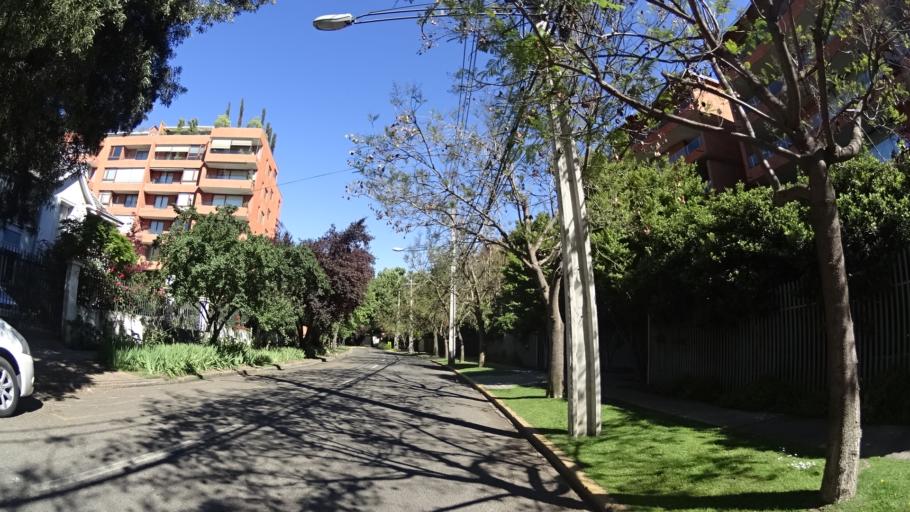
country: CL
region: Santiago Metropolitan
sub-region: Provincia de Santiago
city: Villa Presidente Frei, Nunoa, Santiago, Chile
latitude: -33.3950
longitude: -70.5924
